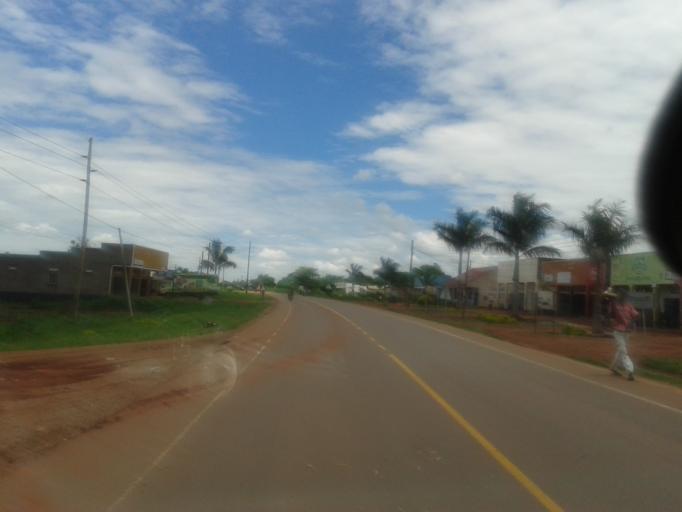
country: UG
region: Western Region
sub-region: Kiryandongo District
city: Kiryandongo
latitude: 1.8070
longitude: 32.0103
